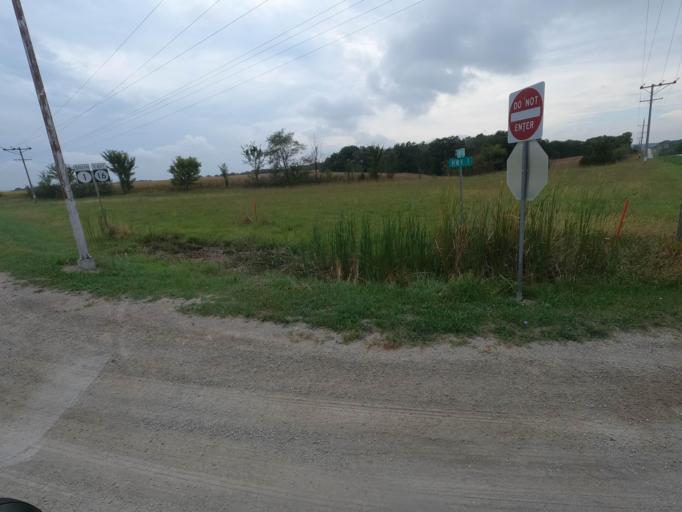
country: US
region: Iowa
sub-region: Van Buren County
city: Keosauqua
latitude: 40.8351
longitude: -91.9492
